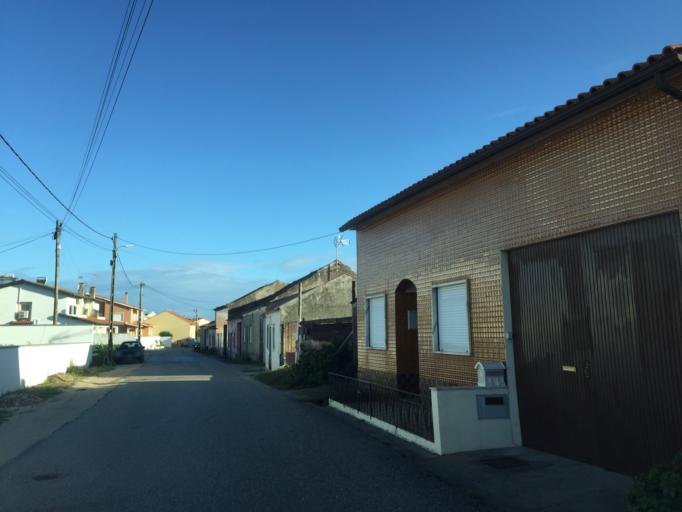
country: PT
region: Coimbra
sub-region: Figueira da Foz
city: Lavos
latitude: 40.0540
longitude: -8.8097
